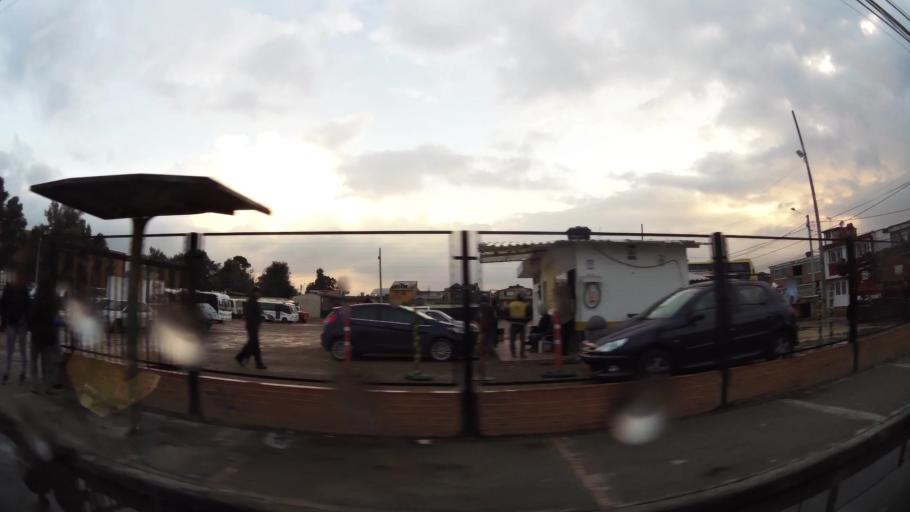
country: CO
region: Cundinamarca
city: Chia
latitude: 4.8566
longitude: -74.0585
